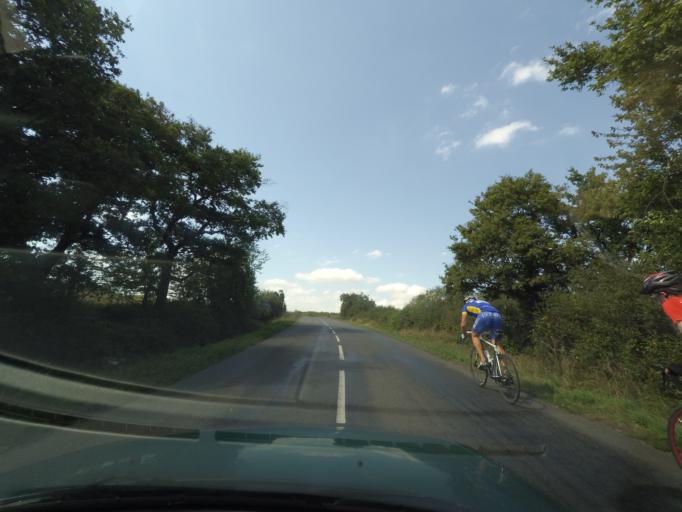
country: FR
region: Pays de la Loire
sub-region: Departement de la Loire-Atlantique
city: Saint-Lumine-de-Coutais
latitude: 47.0568
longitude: -1.7508
